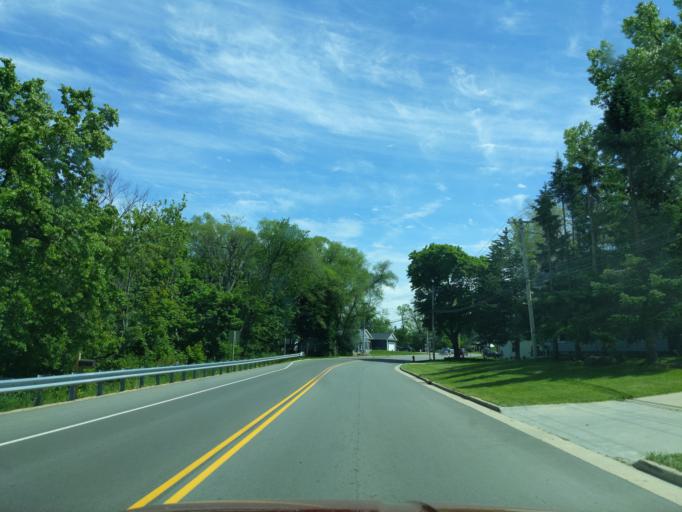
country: US
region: Wisconsin
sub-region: Columbia County
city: Pardeeville
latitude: 43.5447
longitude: -89.3036
